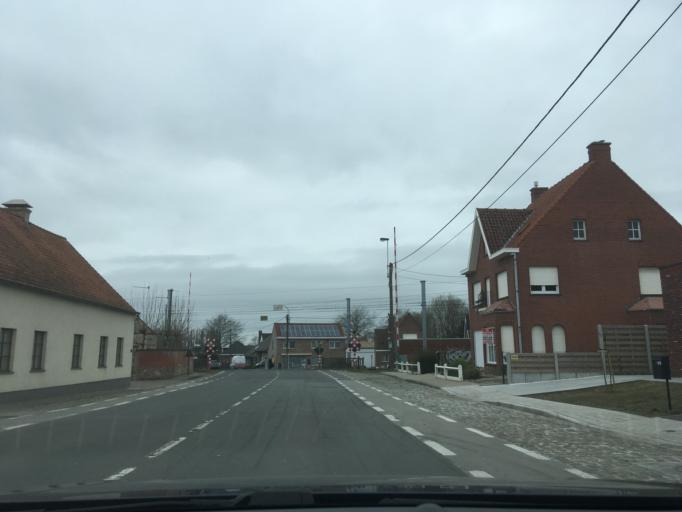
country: BE
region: Flanders
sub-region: Provincie West-Vlaanderen
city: Kortemark
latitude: 51.0265
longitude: 3.0604
